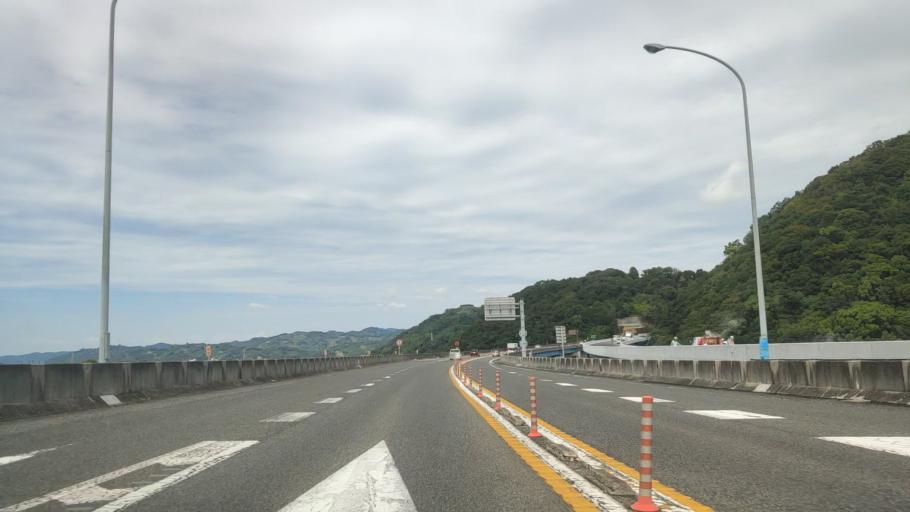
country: JP
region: Wakayama
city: Gobo
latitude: 34.0110
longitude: 135.1903
